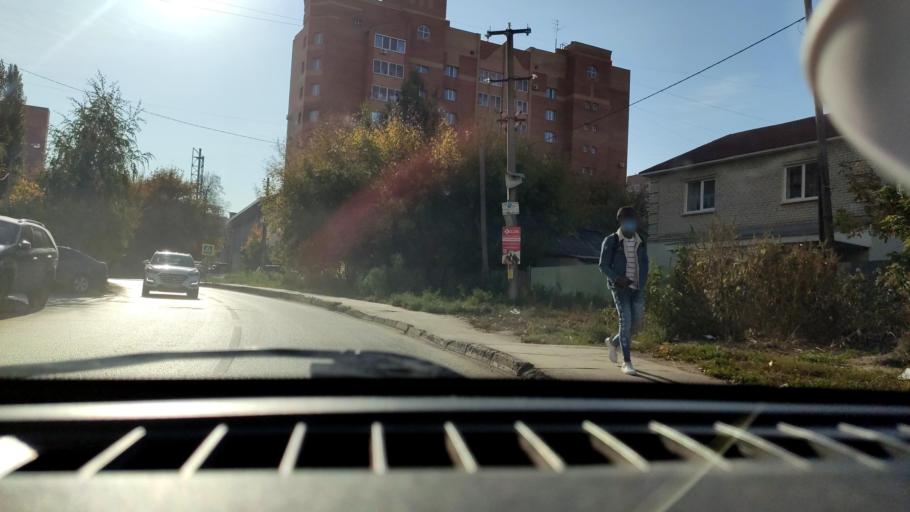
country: RU
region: Samara
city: Samara
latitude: 53.2160
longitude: 50.1670
